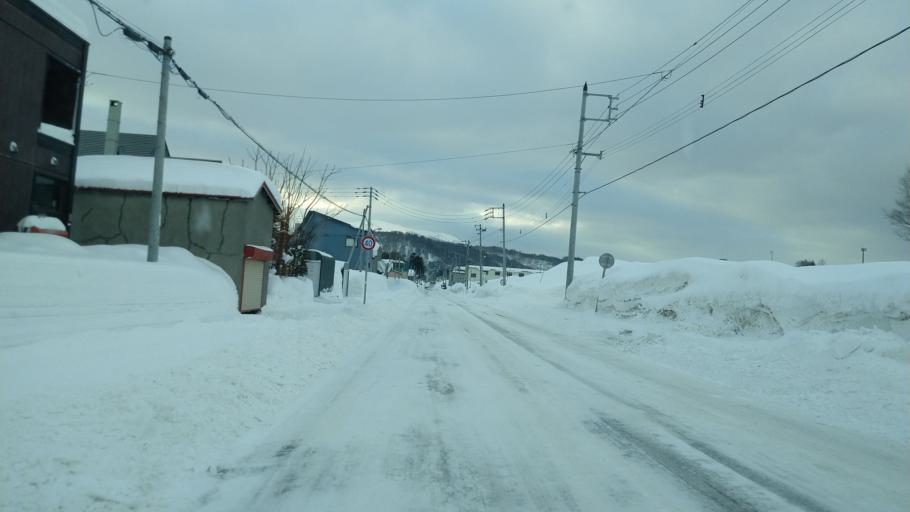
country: JP
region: Hokkaido
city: Niseko Town
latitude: 42.9087
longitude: 140.7587
